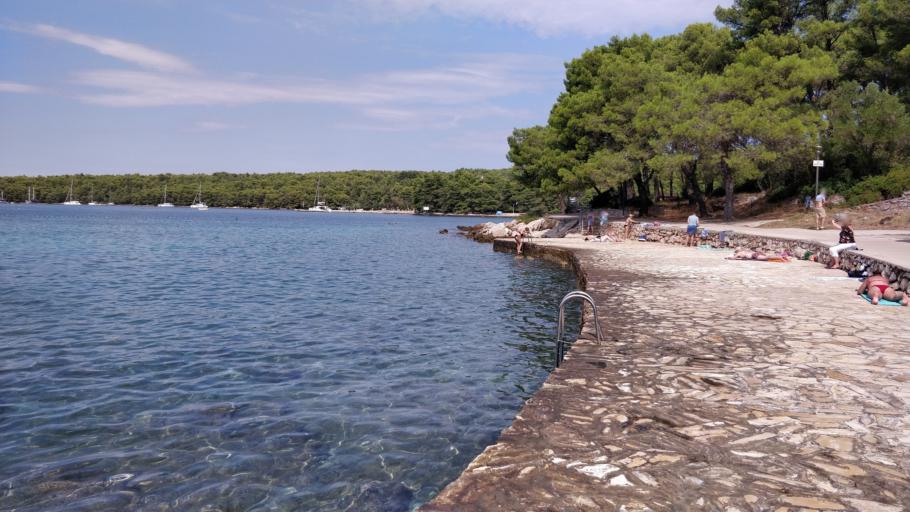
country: HR
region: Splitsko-Dalmatinska
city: Stari Grad
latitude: 43.1829
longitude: 16.5859
